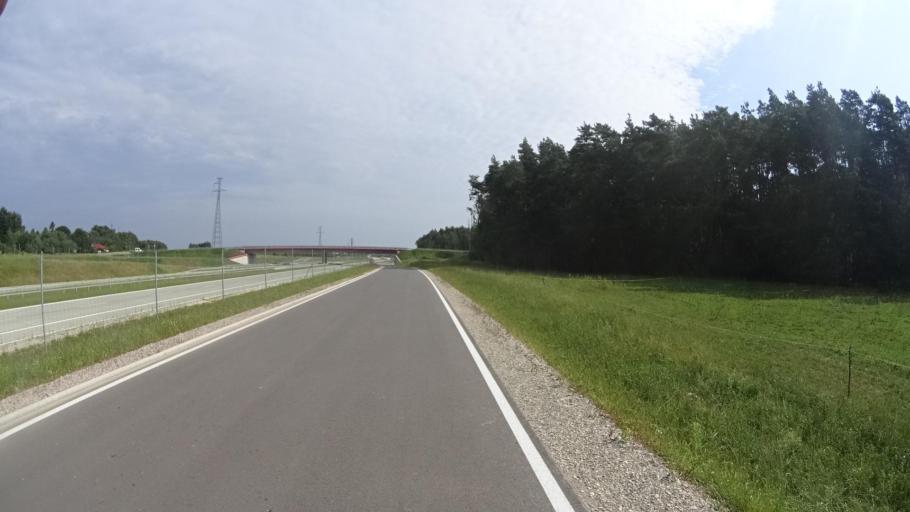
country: PL
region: Masovian Voivodeship
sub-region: Powiat piaseczynski
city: Tarczyn
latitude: 51.9644
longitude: 20.8582
